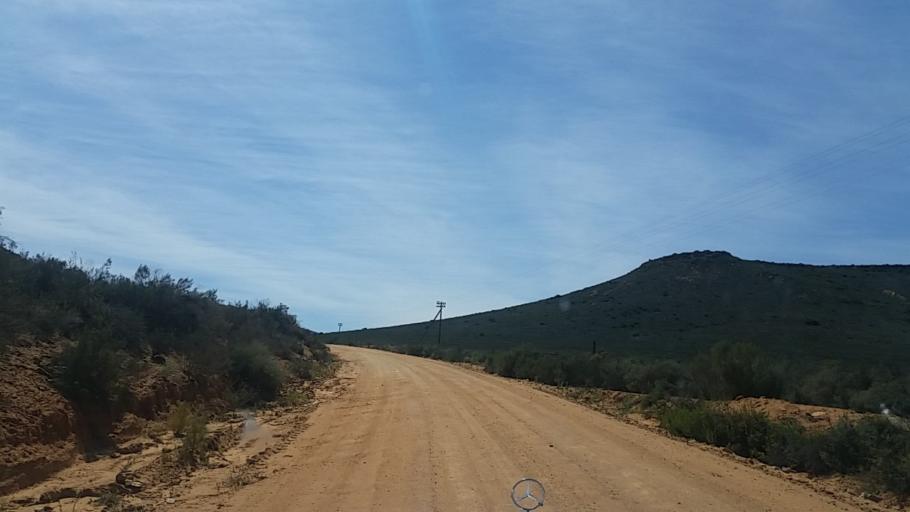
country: ZA
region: Western Cape
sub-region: Eden District Municipality
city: Knysna
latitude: -33.6385
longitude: 23.1501
